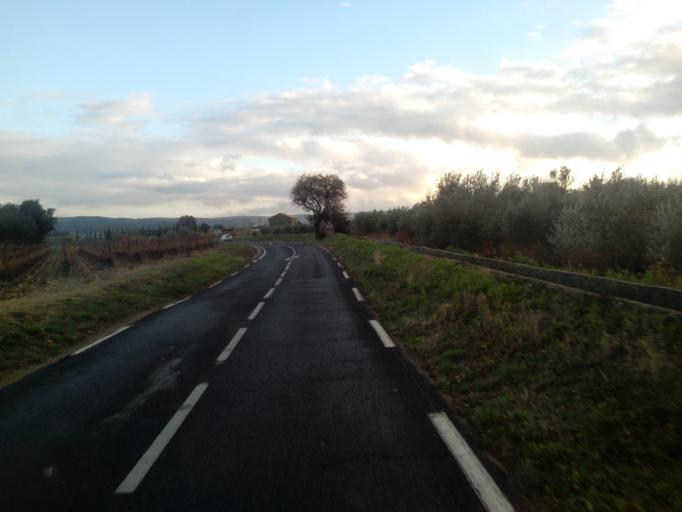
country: FR
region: Languedoc-Roussillon
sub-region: Departement de l'Herault
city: Saint-Jean-de-Fos
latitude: 43.7047
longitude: 3.5616
